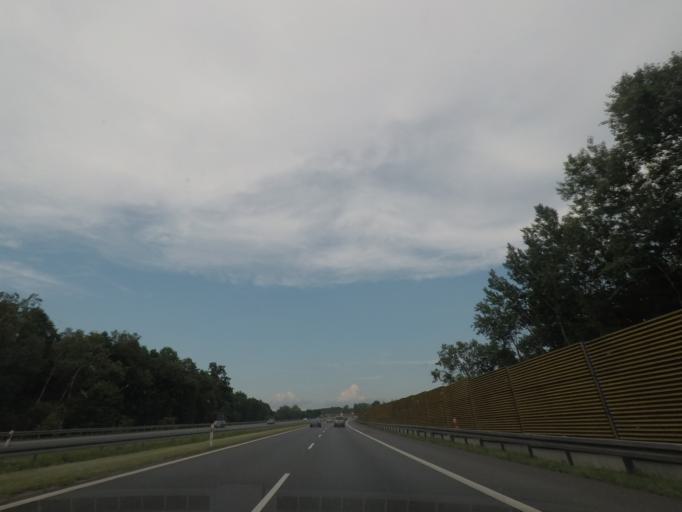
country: PL
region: Lesser Poland Voivodeship
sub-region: Powiat krakowski
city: Zalas
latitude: 50.0920
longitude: 19.6098
